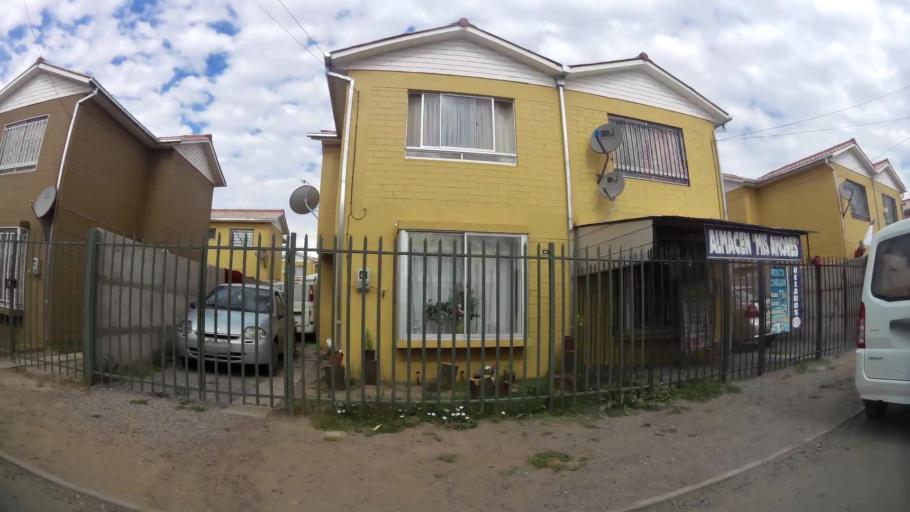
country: CL
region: Santiago Metropolitan
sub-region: Provincia de Santiago
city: La Pintana
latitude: -33.6130
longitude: -70.6198
